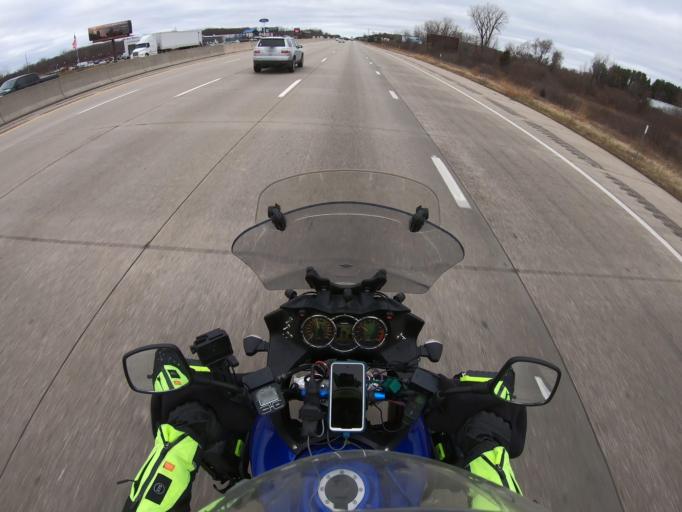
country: US
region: Michigan
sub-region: Saginaw County
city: Birch Run
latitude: 43.2520
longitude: -83.7782
